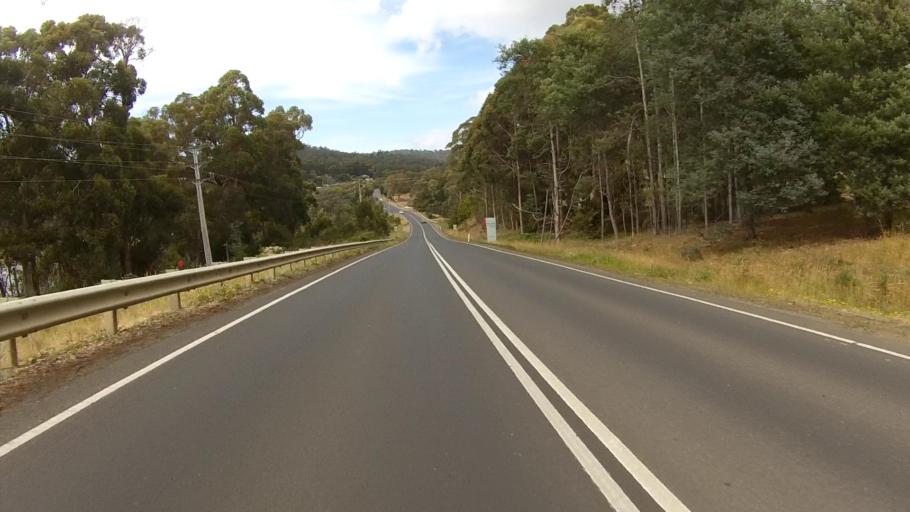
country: AU
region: Tasmania
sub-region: Kingborough
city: Margate
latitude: -43.0702
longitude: 147.2567
